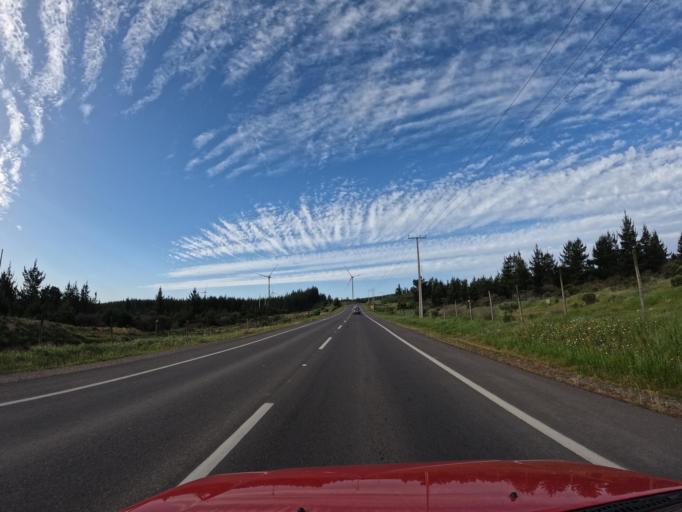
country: CL
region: Valparaiso
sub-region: San Antonio Province
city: San Antonio
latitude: -34.0544
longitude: -71.6247
